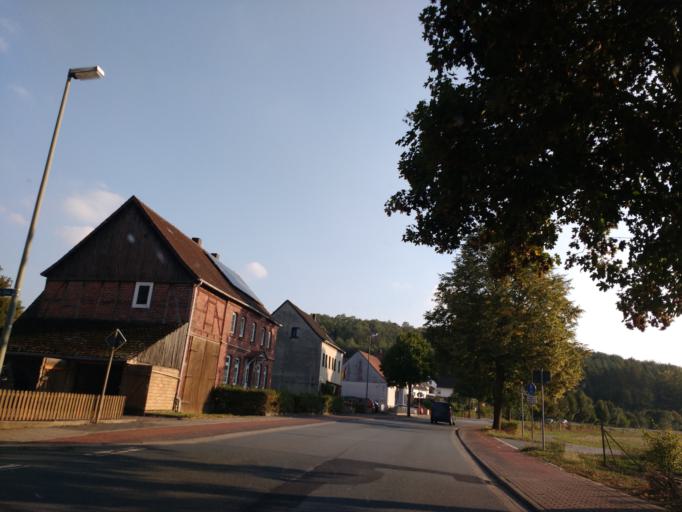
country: DE
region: North Rhine-Westphalia
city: Brakel
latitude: 51.6766
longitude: 9.1642
